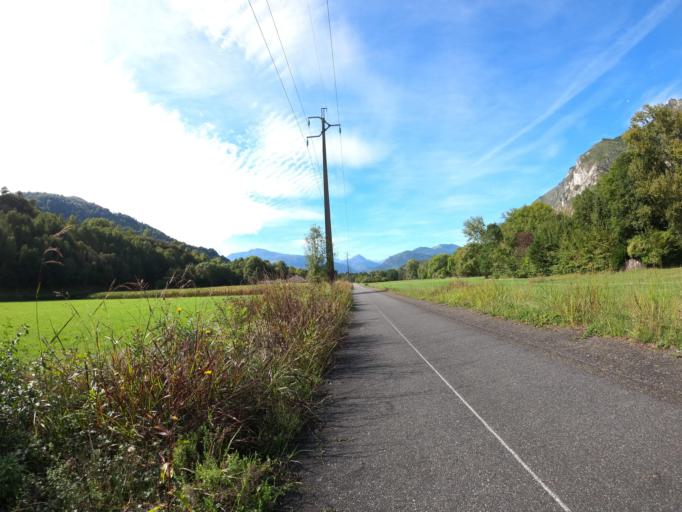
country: FR
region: Midi-Pyrenees
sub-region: Departement des Hautes-Pyrenees
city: Lourdes
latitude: 43.0457
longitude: -0.0539
